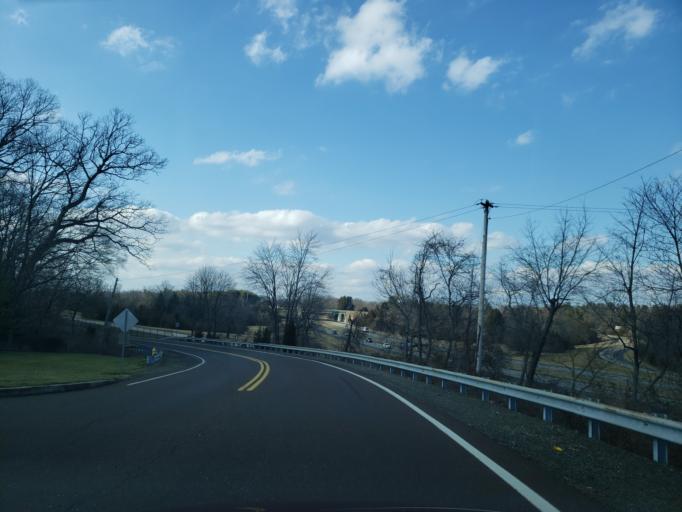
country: US
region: Pennsylvania
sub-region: Bucks County
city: Doylestown
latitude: 40.2909
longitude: -75.1344
